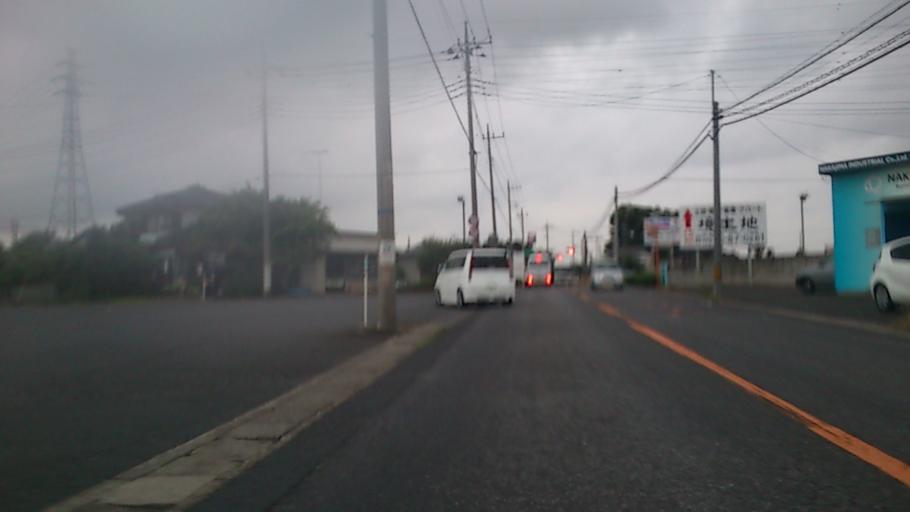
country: JP
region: Ibaraki
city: Sakai
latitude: 36.0987
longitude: 139.8129
